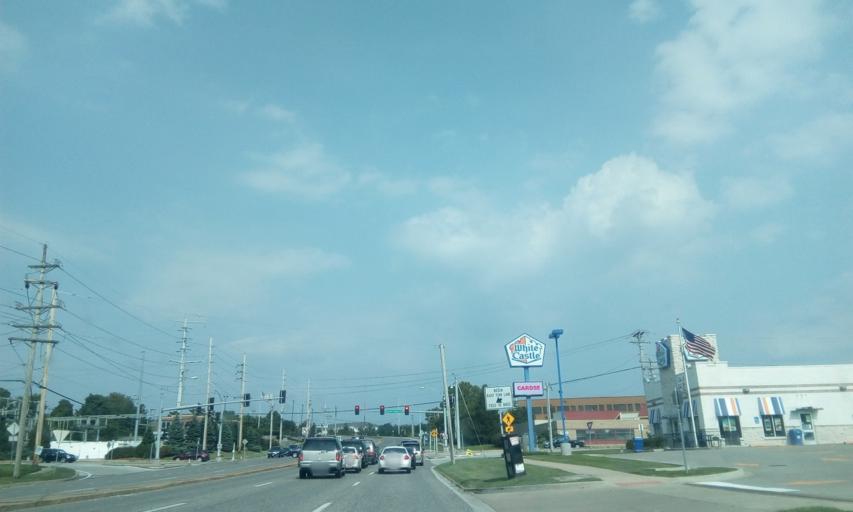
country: US
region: Missouri
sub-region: Saint Louis County
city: Town and Country
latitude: 38.5965
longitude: -90.4749
